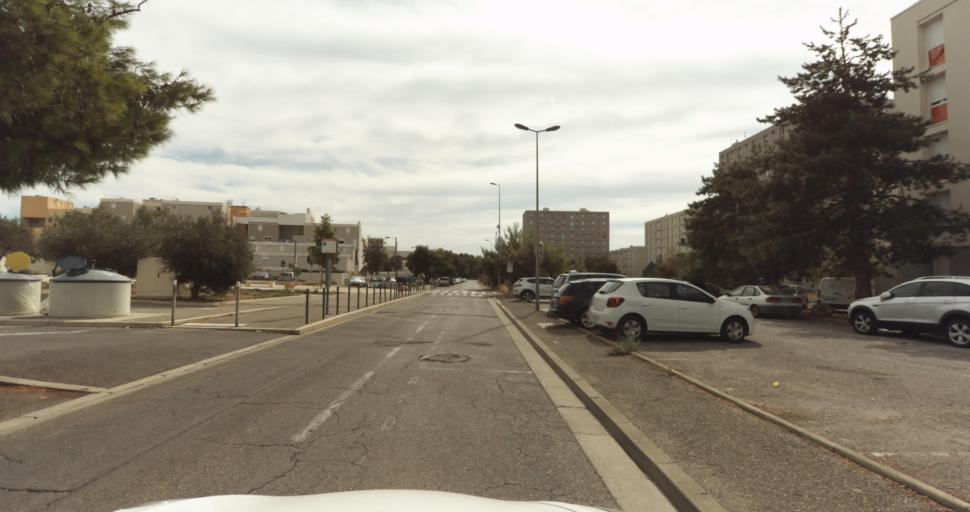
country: FR
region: Provence-Alpes-Cote d'Azur
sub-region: Departement des Bouches-du-Rhone
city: Miramas
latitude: 43.5952
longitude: 5.0077
